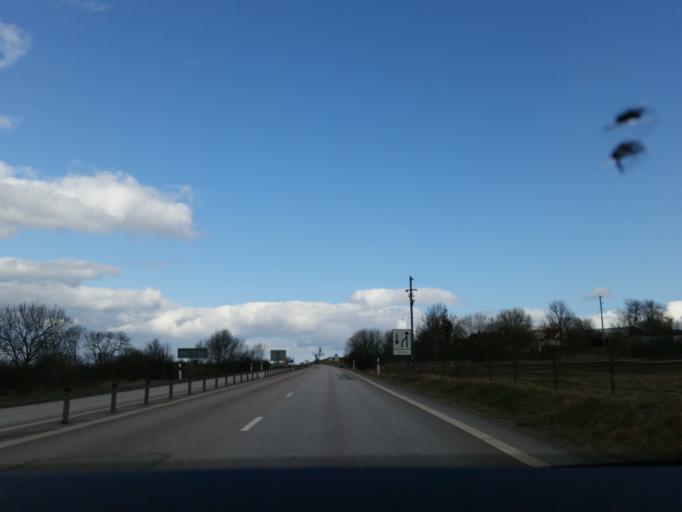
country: SE
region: Kalmar
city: Faerjestaden
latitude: 56.6750
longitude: 16.5183
